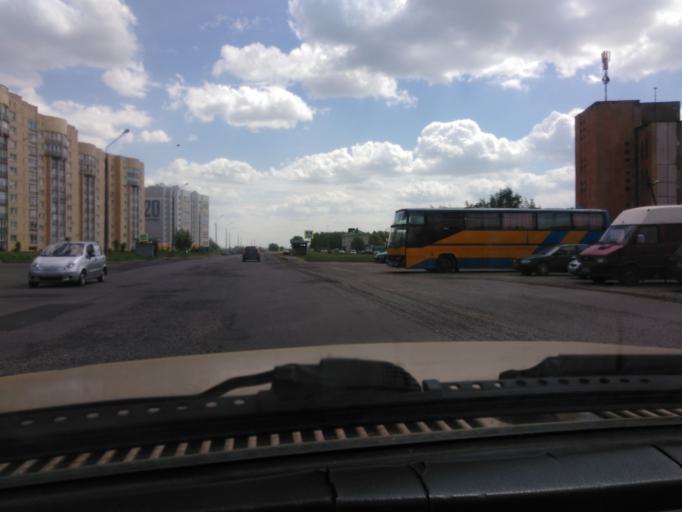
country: BY
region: Mogilev
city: Mahilyow
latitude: 53.9451
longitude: 30.3630
